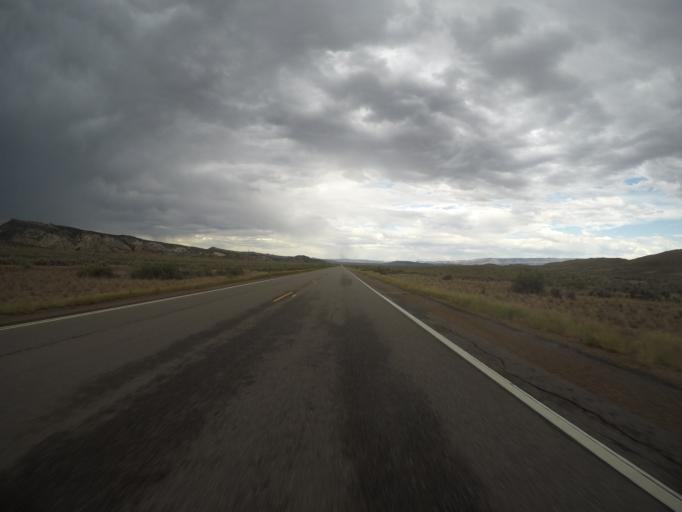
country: US
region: Colorado
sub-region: Rio Blanco County
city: Rangely
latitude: 40.2508
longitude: -108.7850
